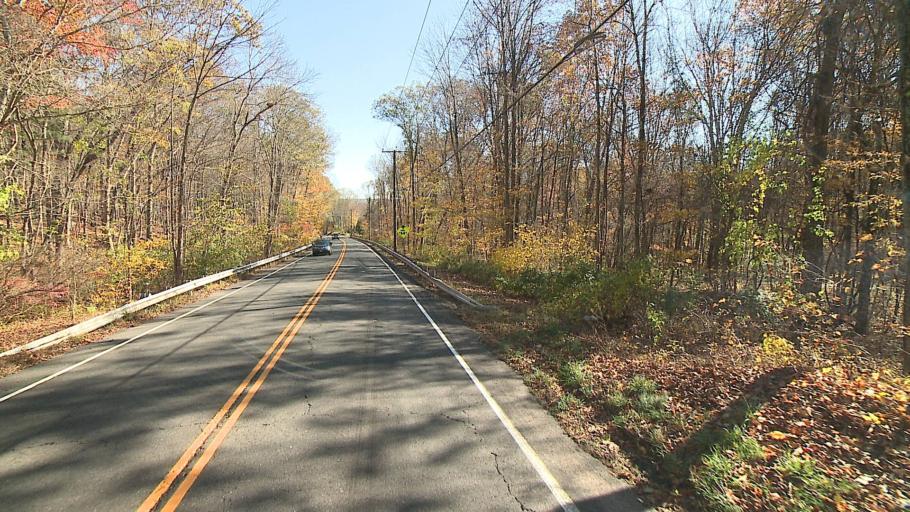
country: US
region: Connecticut
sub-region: Tolland County
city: Coventry Lake
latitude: 41.7981
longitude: -72.3242
